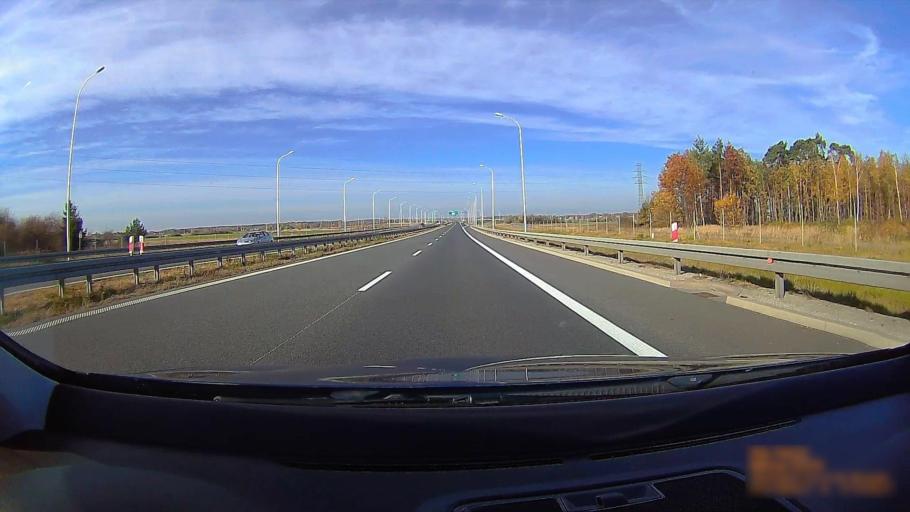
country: PL
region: Greater Poland Voivodeship
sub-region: Powiat ostrowski
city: Ostrow Wielkopolski
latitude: 51.6595
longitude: 17.8617
